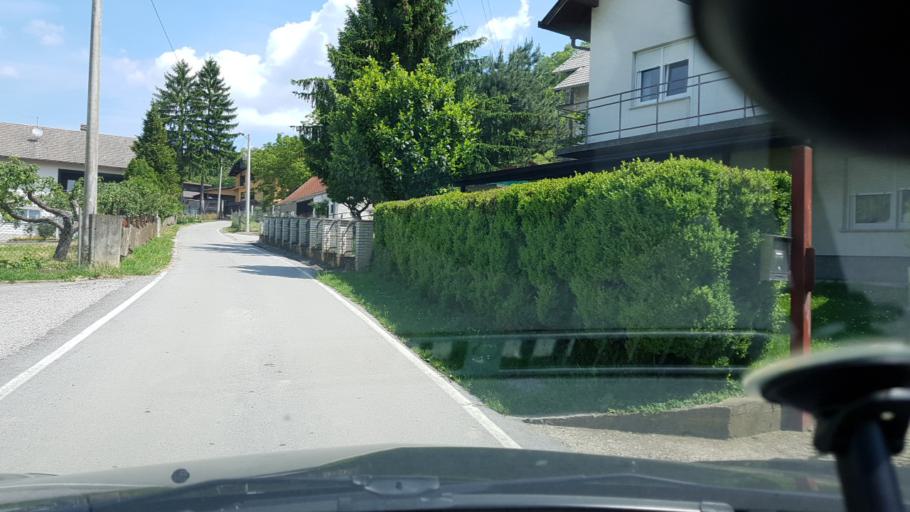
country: HR
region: Krapinsko-Zagorska
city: Marija Bistrica
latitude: 45.9333
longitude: 16.1789
